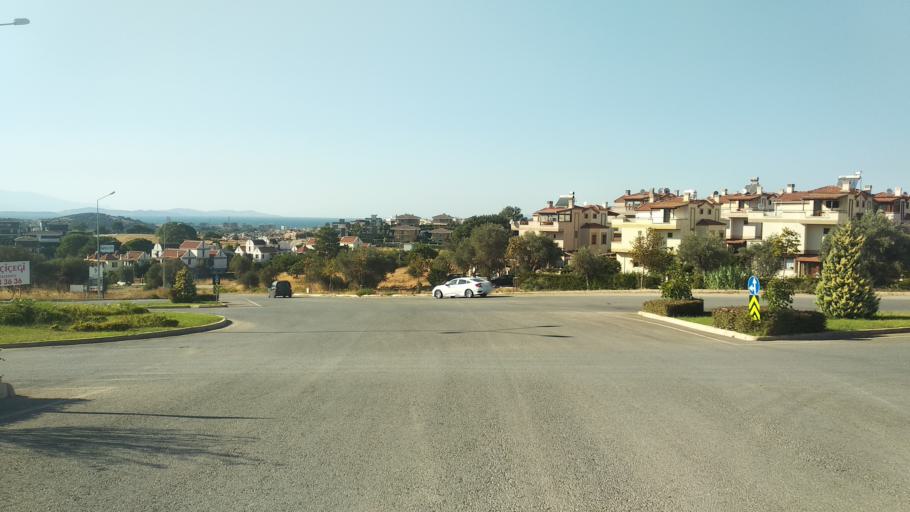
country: TR
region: Izmir
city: Urla
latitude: 38.3601
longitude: 26.8794
